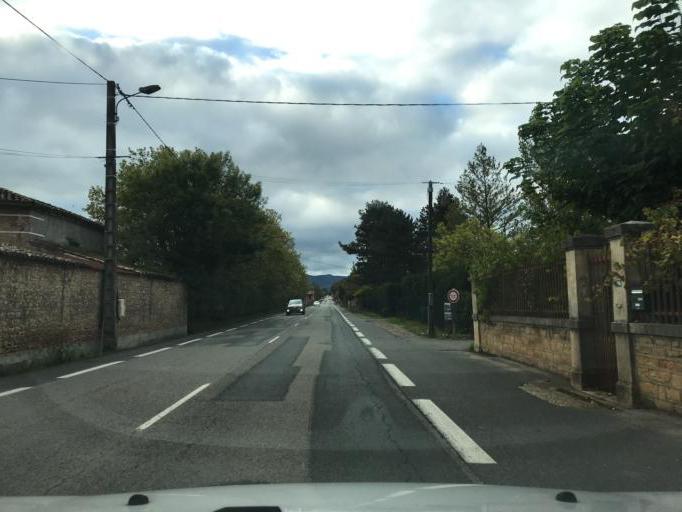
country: FR
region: Rhone-Alpes
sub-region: Departement du Rhone
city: Gleize
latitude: 45.9933
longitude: 4.6855
